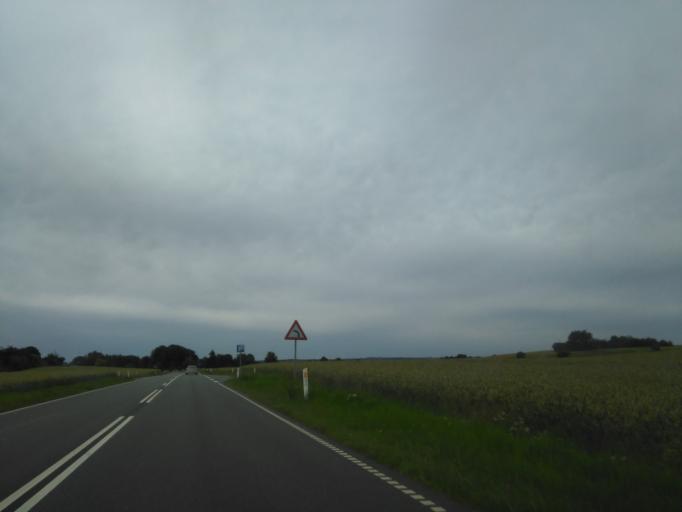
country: DK
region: Central Jutland
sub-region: Arhus Kommune
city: Solbjerg
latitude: 56.0185
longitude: 10.0411
